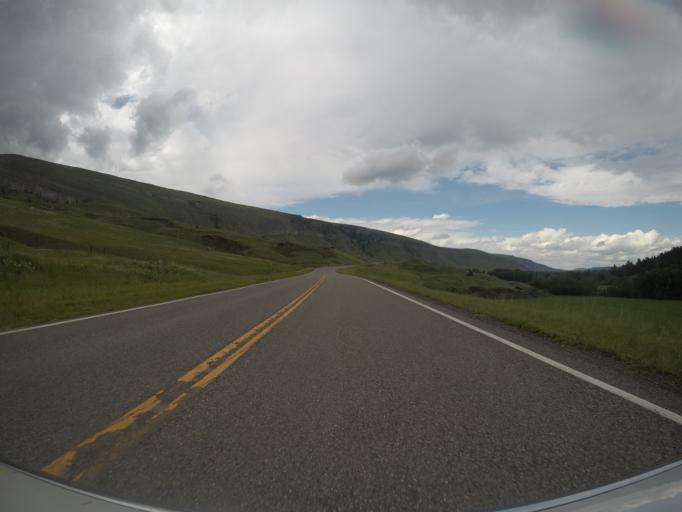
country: US
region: Montana
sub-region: Sweet Grass County
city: Big Timber
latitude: 45.5630
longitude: -110.2019
